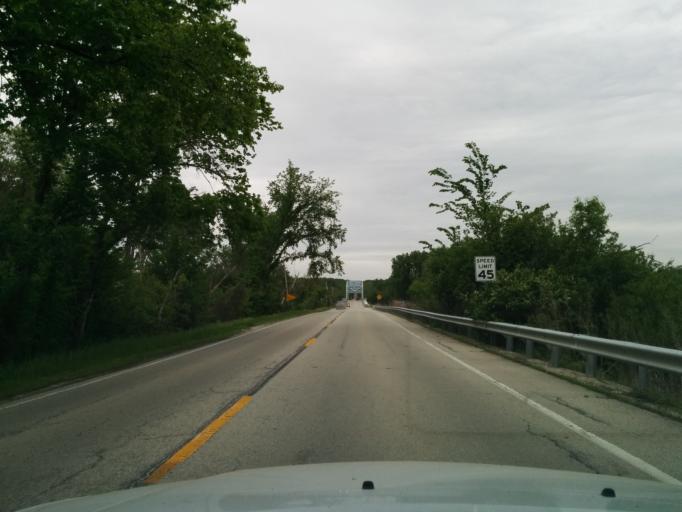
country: US
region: Illinois
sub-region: Cook County
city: Palos Park
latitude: 41.6915
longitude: -87.8751
